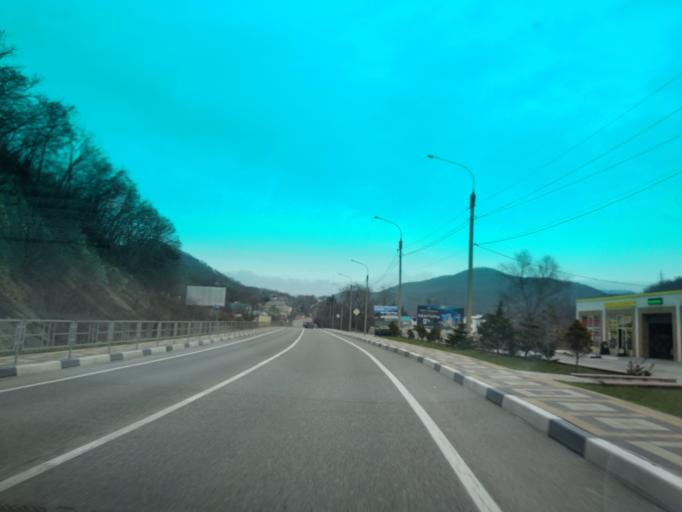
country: RU
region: Krasnodarskiy
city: Ol'ginka
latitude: 44.2070
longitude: 38.8911
